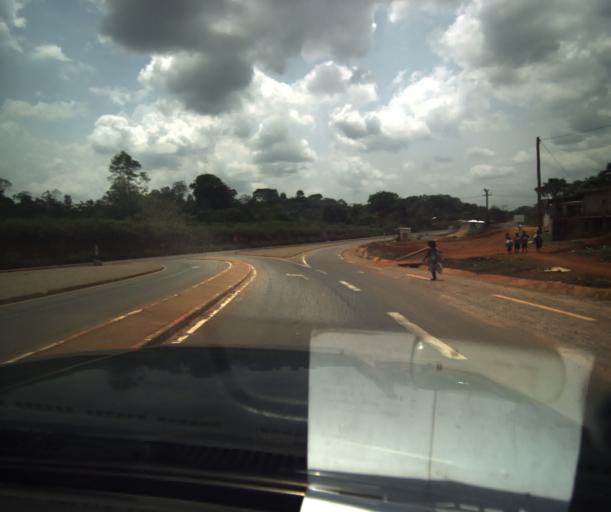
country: CM
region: Centre
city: Mbankomo
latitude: 3.7901
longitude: 11.4426
